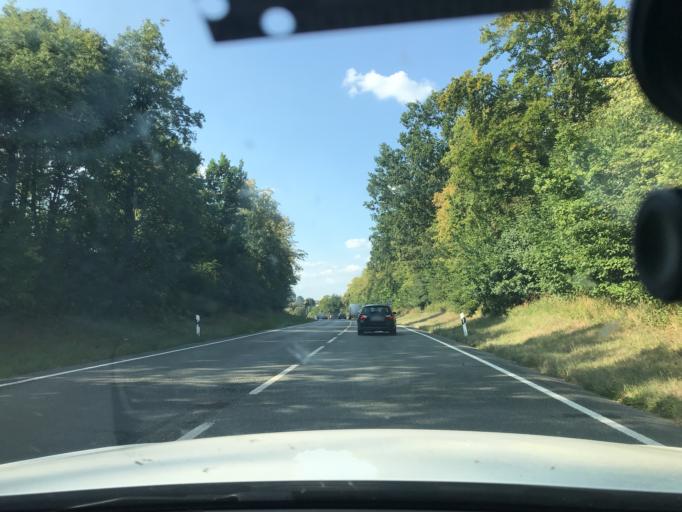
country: DE
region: Bavaria
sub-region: Upper Palatinate
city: Sulzbach-Rosenberg
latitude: 49.4939
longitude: 11.7319
